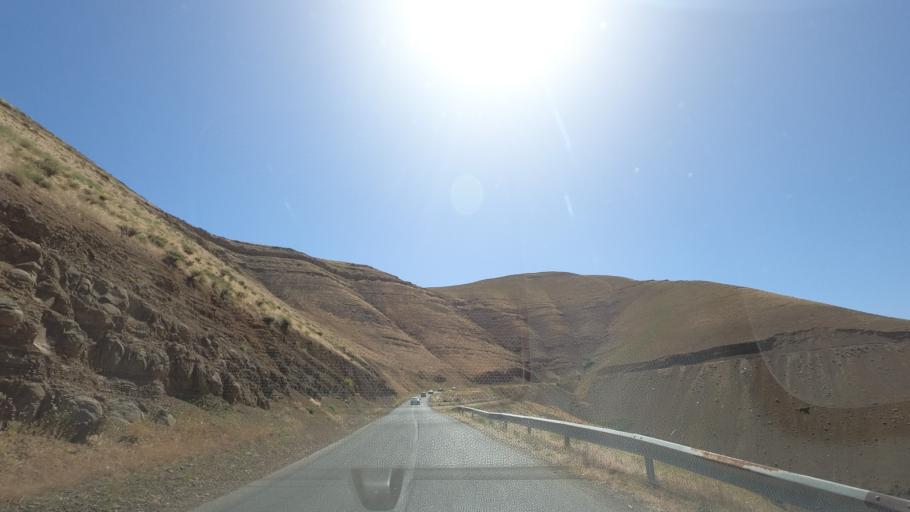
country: IR
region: Alborz
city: Karaj
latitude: 35.9326
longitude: 51.0830
